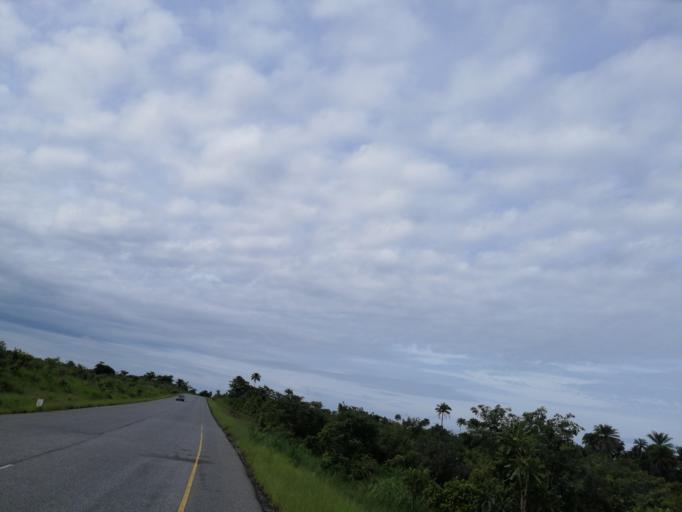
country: SL
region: Northern Province
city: Port Loko
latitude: 8.7792
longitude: -12.8572
